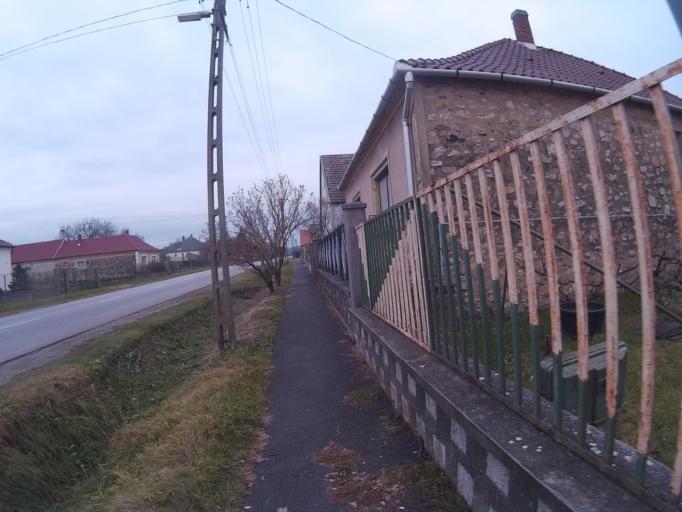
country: HU
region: Veszprem
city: Devecser
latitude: 47.0012
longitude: 17.4558
